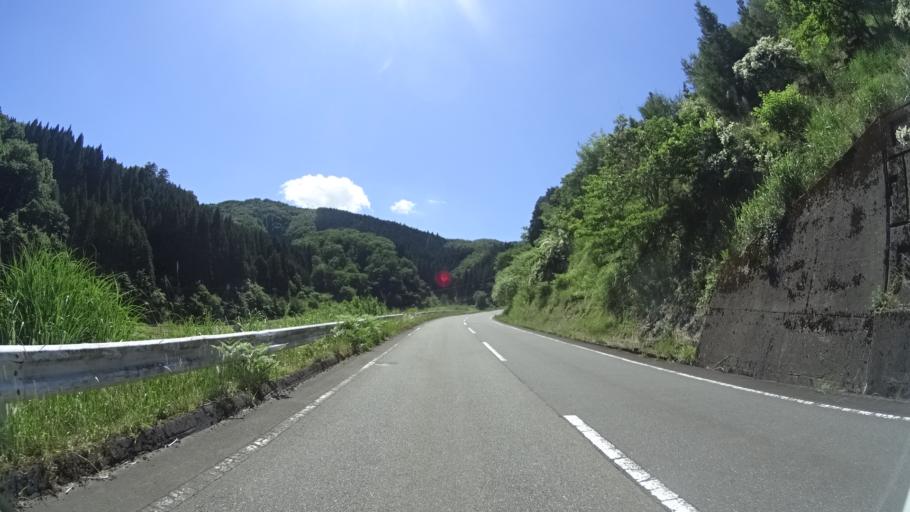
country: JP
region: Kyoto
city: Fukuchiyama
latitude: 35.4239
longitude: 135.0623
